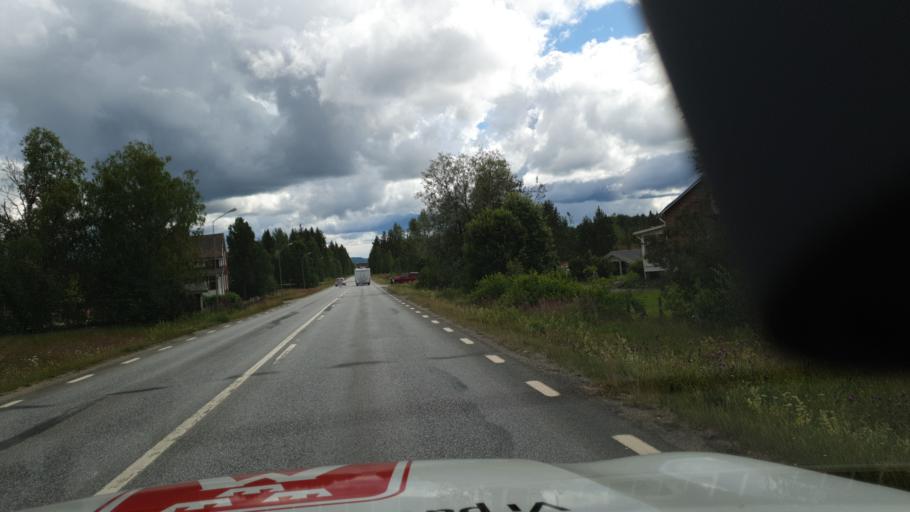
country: SE
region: Vaesterbotten
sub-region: Vannas Kommun
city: Vaennaes
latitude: 63.9625
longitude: 19.7518
